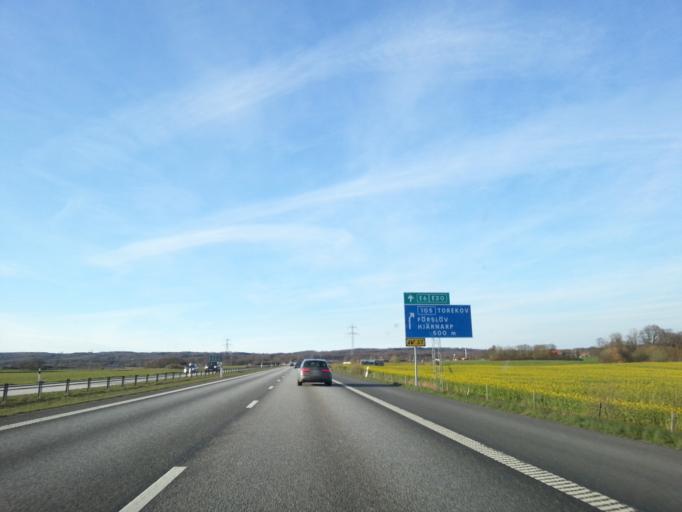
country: SE
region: Skane
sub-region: Angelholms Kommun
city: AEngelholm
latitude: 56.3063
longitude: 12.9089
